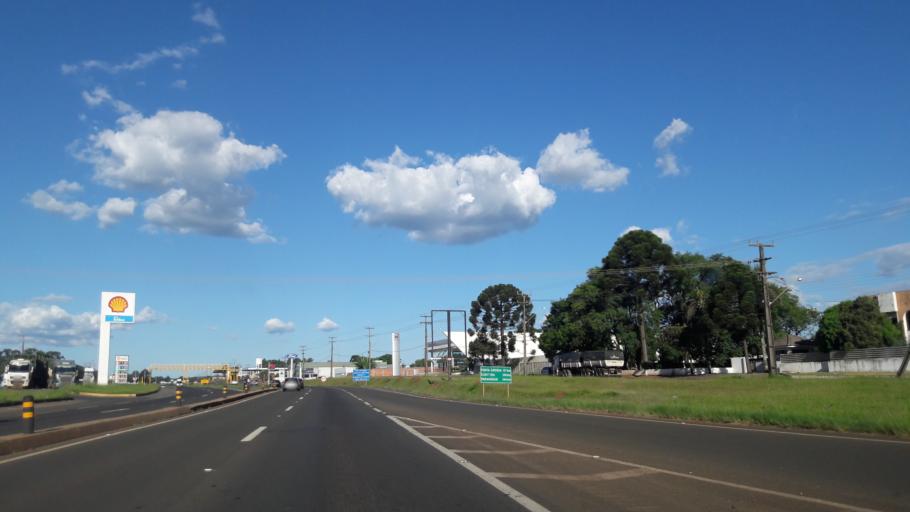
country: BR
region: Parana
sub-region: Guarapuava
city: Guarapuava
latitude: -25.3637
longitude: -51.4735
